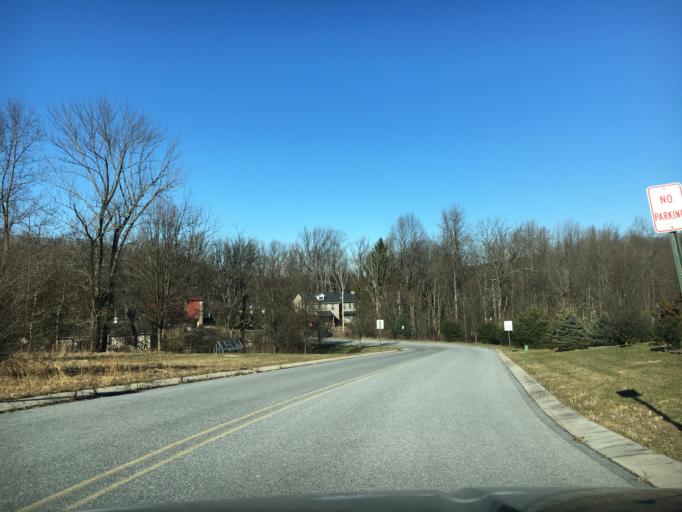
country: US
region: Pennsylvania
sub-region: Berks County
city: Fleetwood
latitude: 40.4304
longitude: -75.8102
